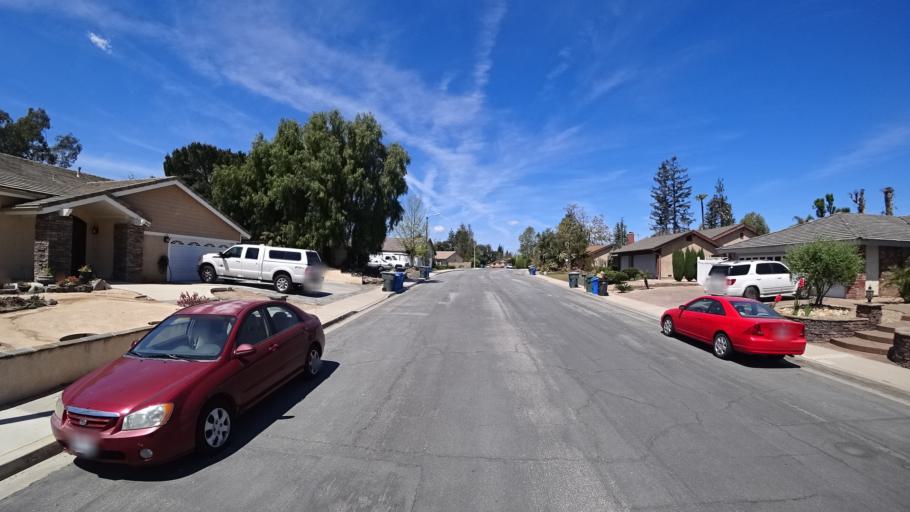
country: US
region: California
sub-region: Ventura County
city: Thousand Oaks
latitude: 34.2196
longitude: -118.8725
